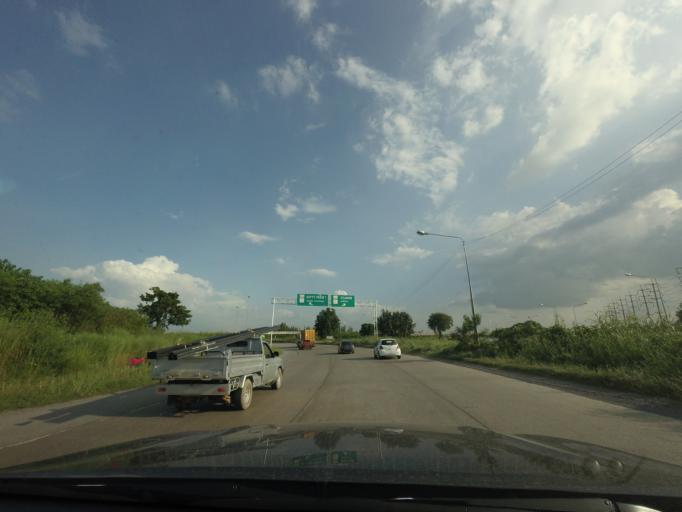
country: TH
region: Sara Buri
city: Saraburi
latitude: 14.5664
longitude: 100.9042
